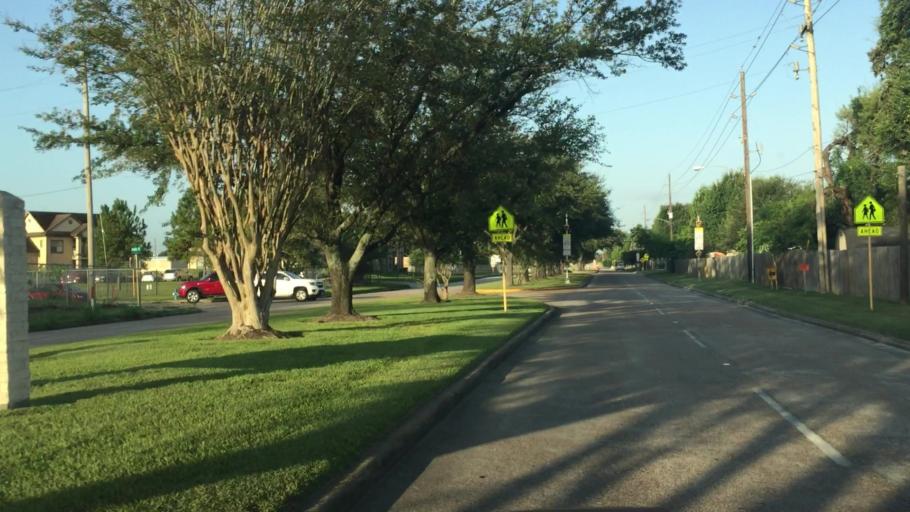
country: US
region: Texas
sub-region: Harris County
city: Hudson
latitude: 29.9477
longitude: -95.4699
